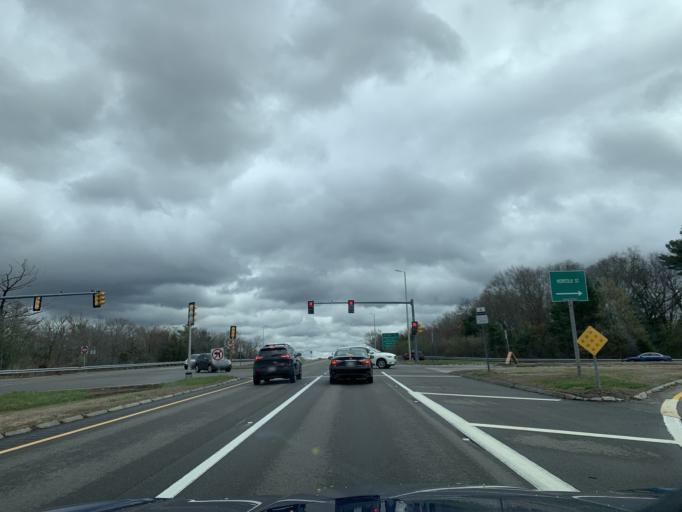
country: US
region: Massachusetts
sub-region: Bristol County
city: Mansfield Center
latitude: 42.0220
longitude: -71.2300
